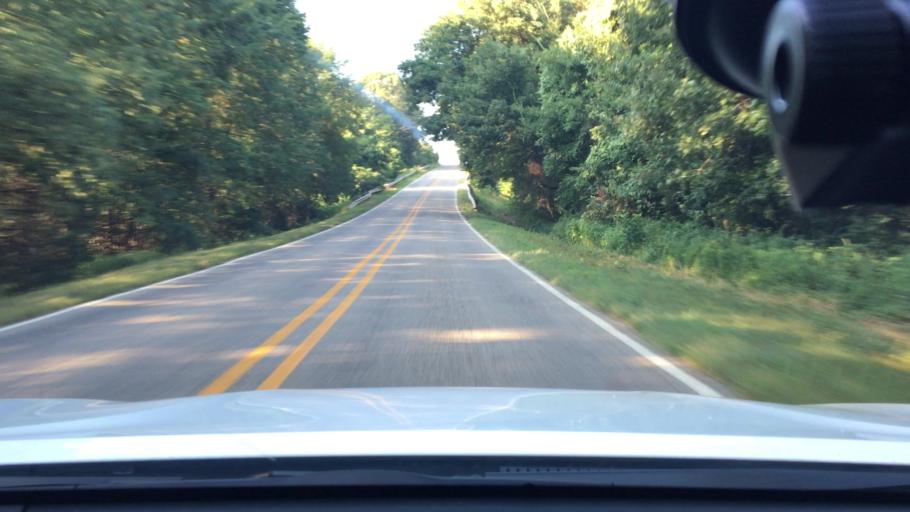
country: US
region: Arkansas
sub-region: Logan County
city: Paris
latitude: 35.3150
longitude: -93.6325
